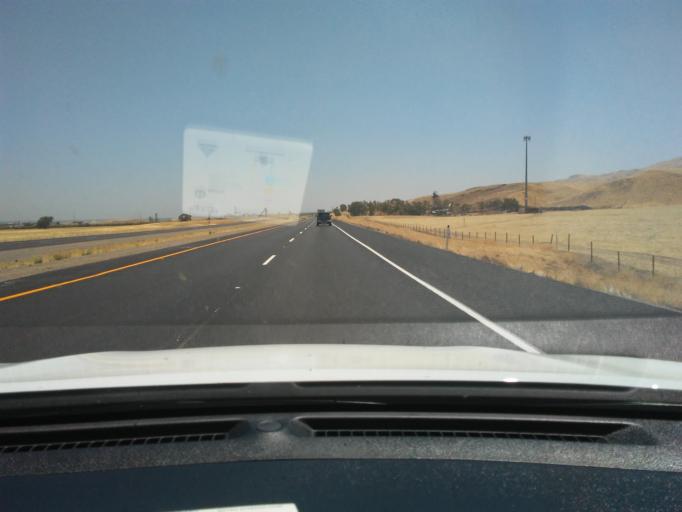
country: US
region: California
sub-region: San Joaquin County
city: Tracy
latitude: 37.6215
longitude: -121.3735
